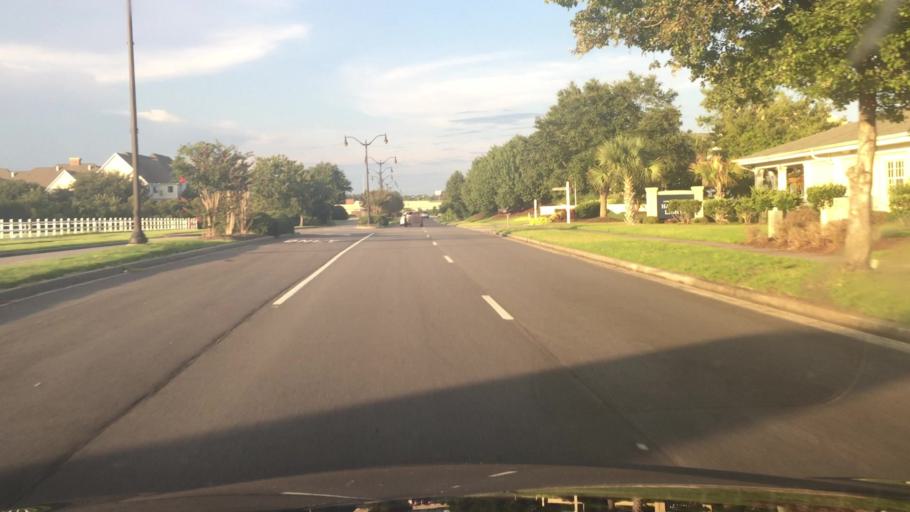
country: US
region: South Carolina
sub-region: Horry County
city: Forestbrook
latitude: 33.7118
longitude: -78.9306
